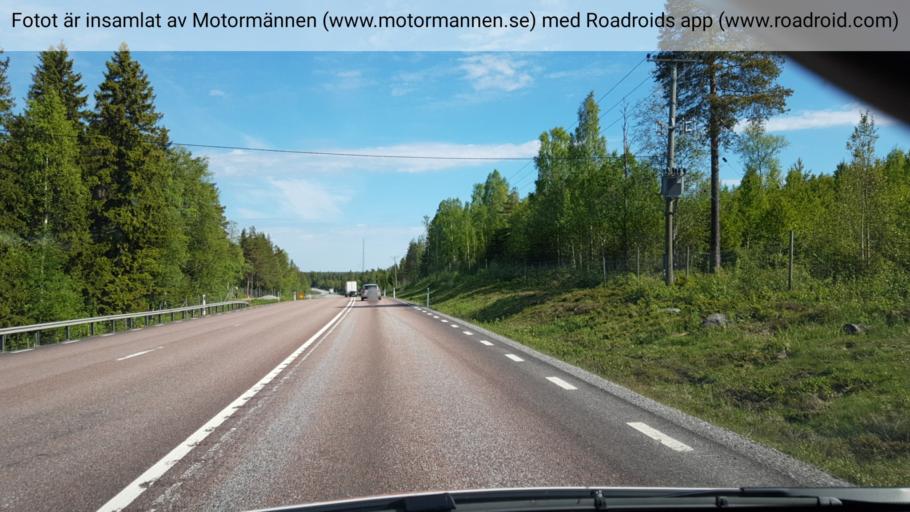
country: SE
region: Vaesterbotten
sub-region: Skelleftea Kommun
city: Burea
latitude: 64.4601
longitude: 21.2905
